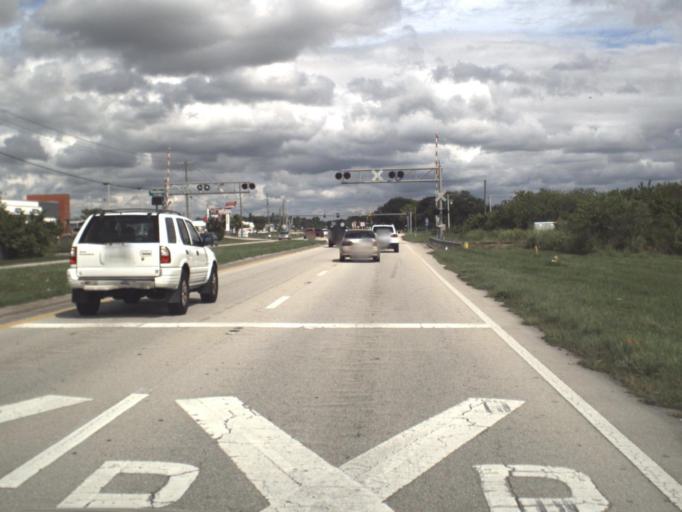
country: US
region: Florida
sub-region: Manatee County
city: Ellenton
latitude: 27.5211
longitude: -82.5452
